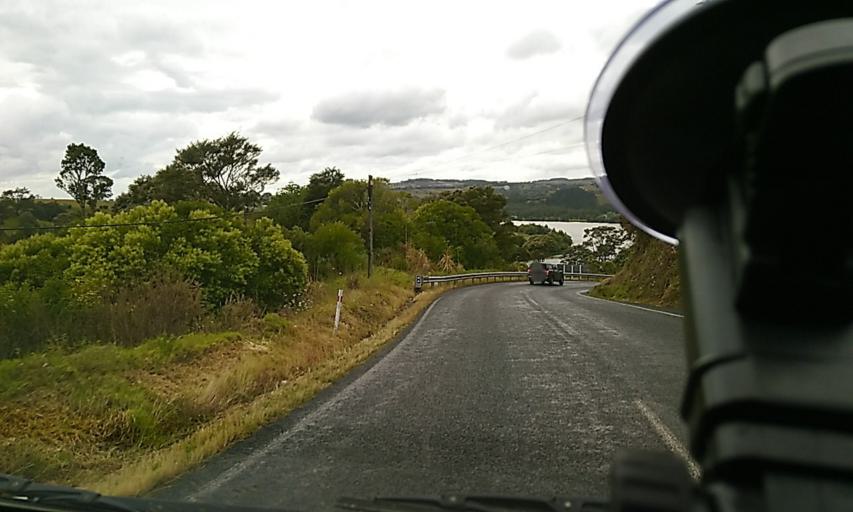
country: NZ
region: Auckland
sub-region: Auckland
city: Pukekohe East
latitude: -37.2986
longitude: 174.9433
